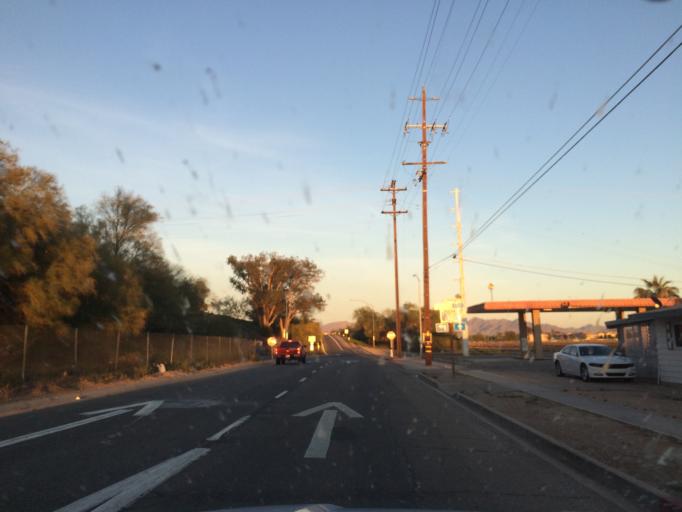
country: US
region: California
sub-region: Riverside County
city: Blythe
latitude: 33.6068
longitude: -114.5889
